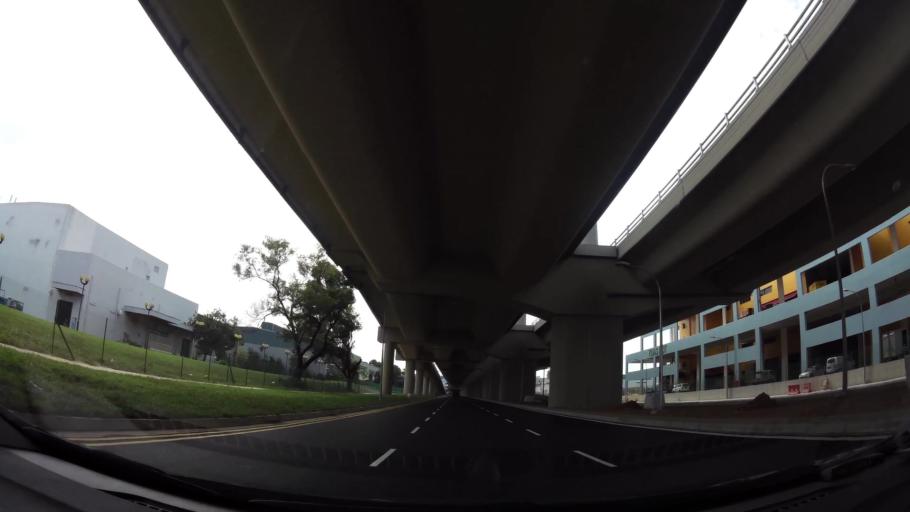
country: MY
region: Johor
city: Johor Bahru
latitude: 1.3264
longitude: 103.6435
